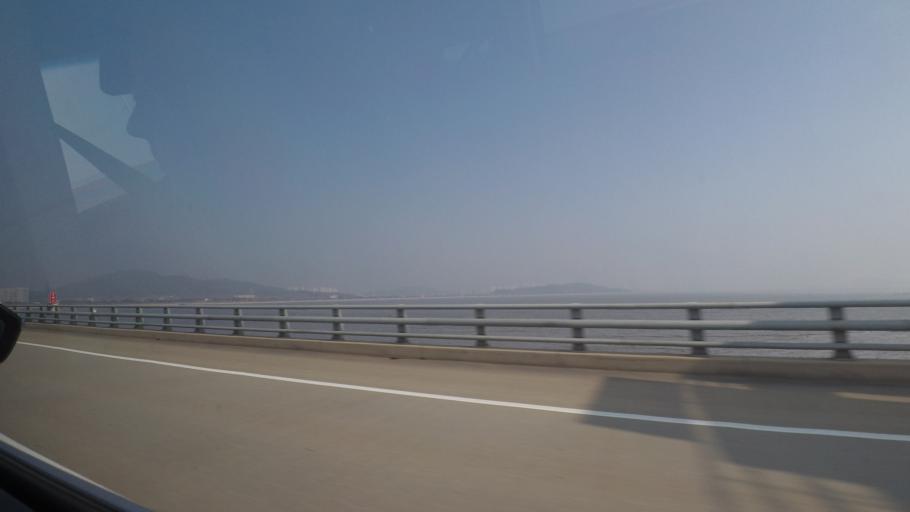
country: KR
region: Incheon
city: Incheon
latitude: 37.4579
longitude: 126.5223
